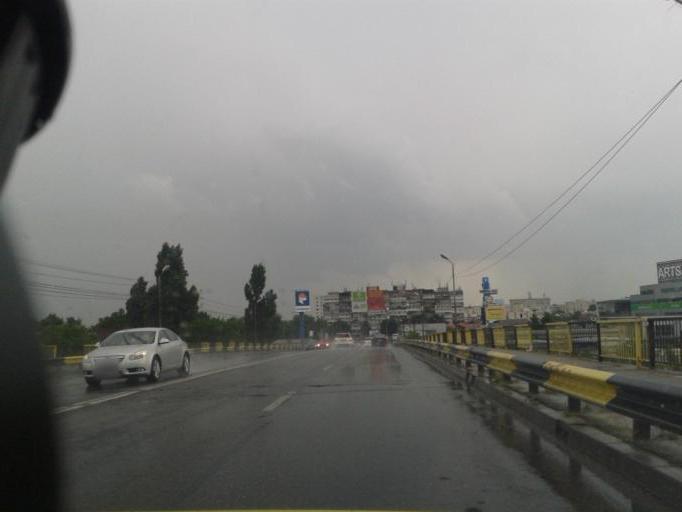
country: RO
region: Prahova
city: Ploiesti
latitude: 44.9486
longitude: 26.0387
